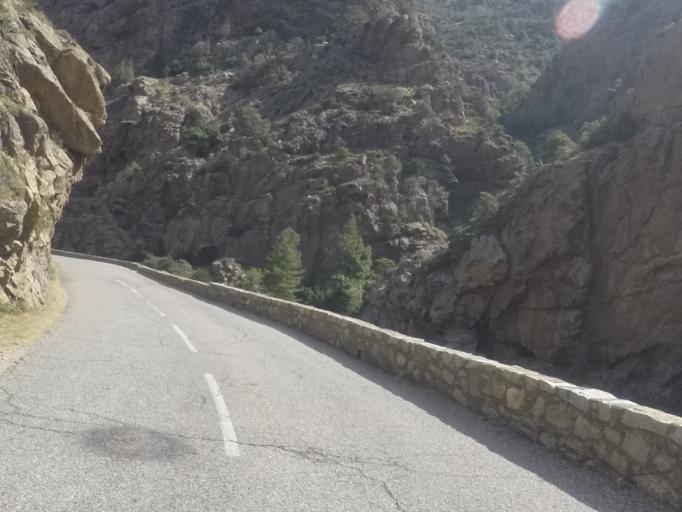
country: FR
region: Corsica
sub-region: Departement de la Haute-Corse
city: Corte
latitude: 42.3688
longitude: 9.0744
